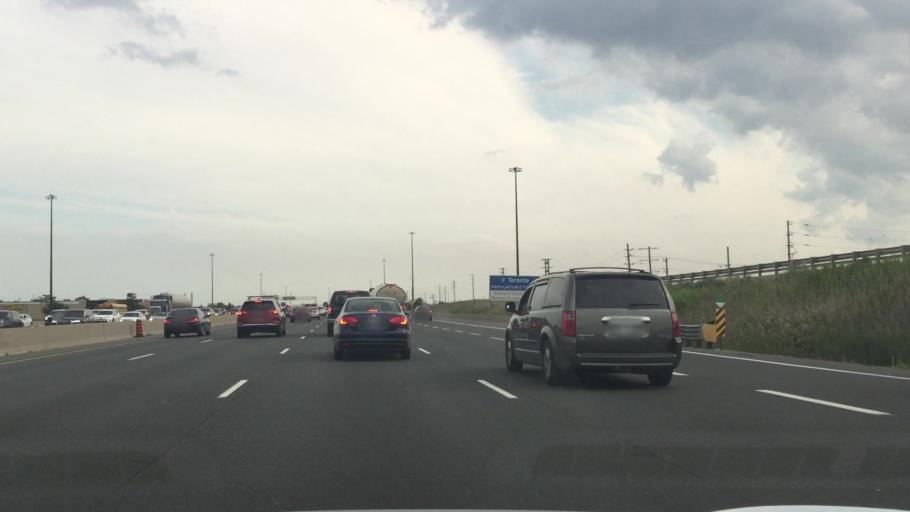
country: CA
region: Ontario
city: Concord
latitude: 43.7741
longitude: -79.5355
